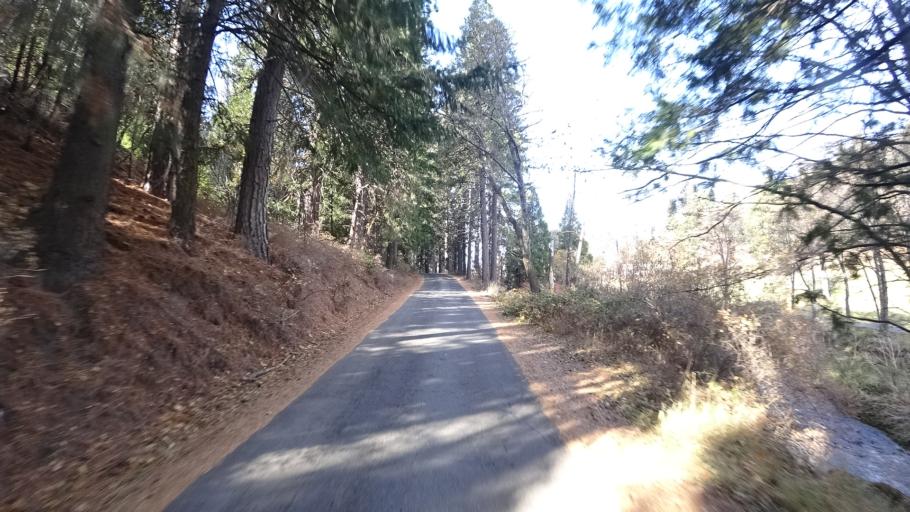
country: US
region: California
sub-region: Siskiyou County
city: Weed
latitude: 41.4308
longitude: -122.3987
